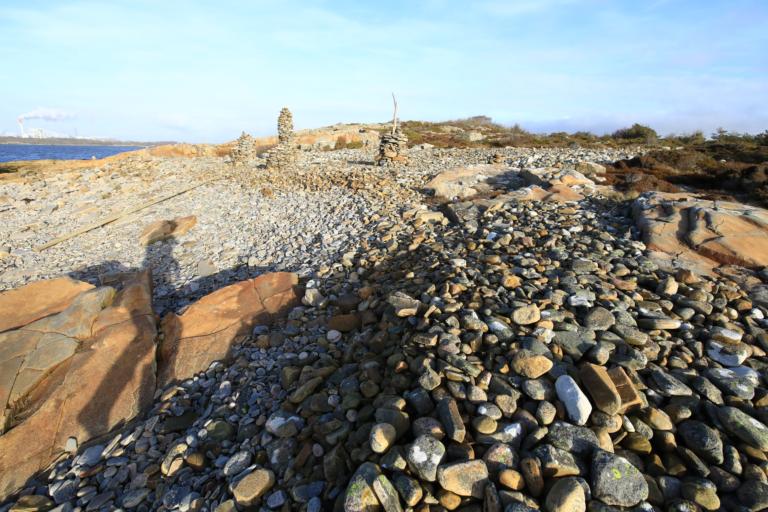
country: SE
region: Halland
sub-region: Kungsbacka Kommun
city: Frillesas
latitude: 57.1991
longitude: 12.1653
